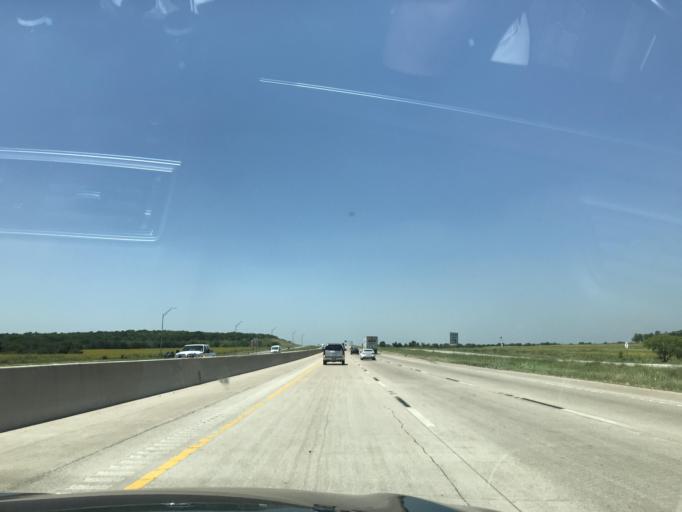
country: US
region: Texas
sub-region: Bell County
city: Salado
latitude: 30.8995
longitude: -97.5634
